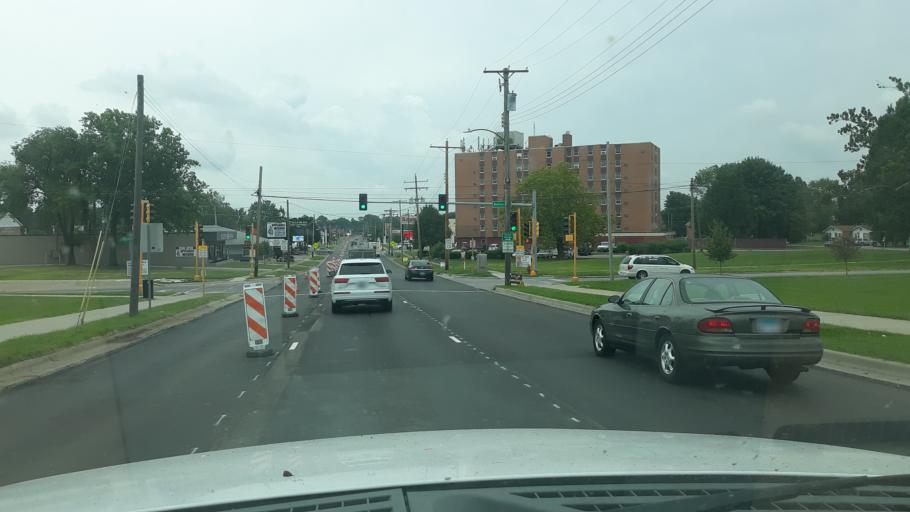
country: US
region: Illinois
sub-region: Jackson County
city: Carbondale
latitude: 37.7253
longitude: -89.2157
